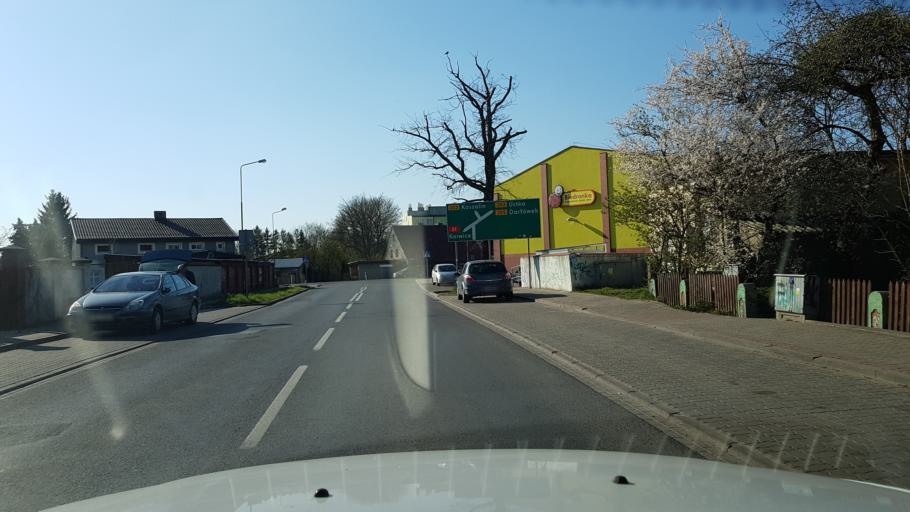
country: PL
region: West Pomeranian Voivodeship
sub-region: Powiat slawienski
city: Darlowo
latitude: 54.4149
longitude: 16.4120
